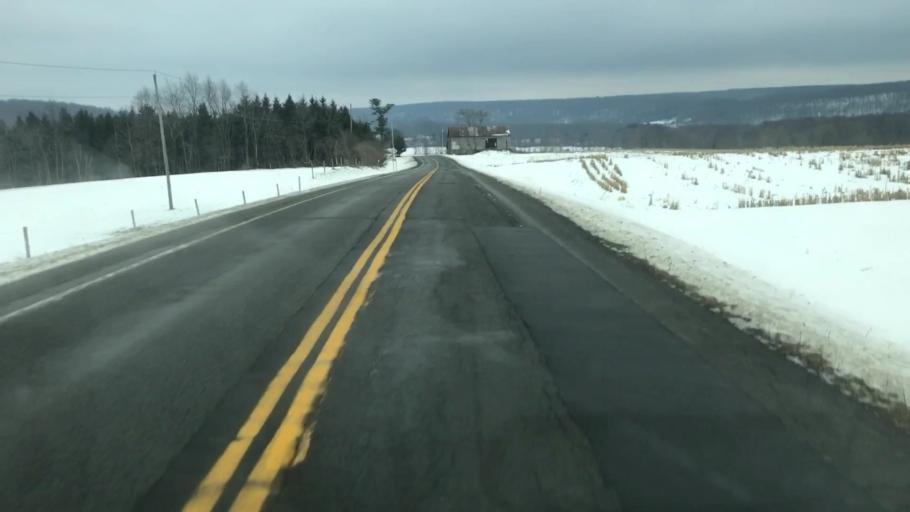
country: US
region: New York
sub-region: Cayuga County
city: Moravia
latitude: 42.7129
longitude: -76.3125
